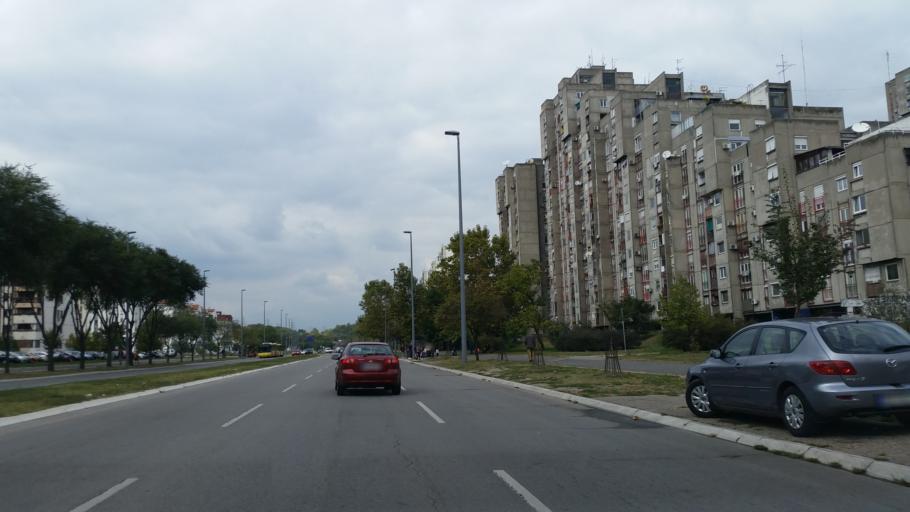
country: RS
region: Central Serbia
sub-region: Belgrade
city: Cukarica
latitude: 44.7985
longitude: 20.3709
